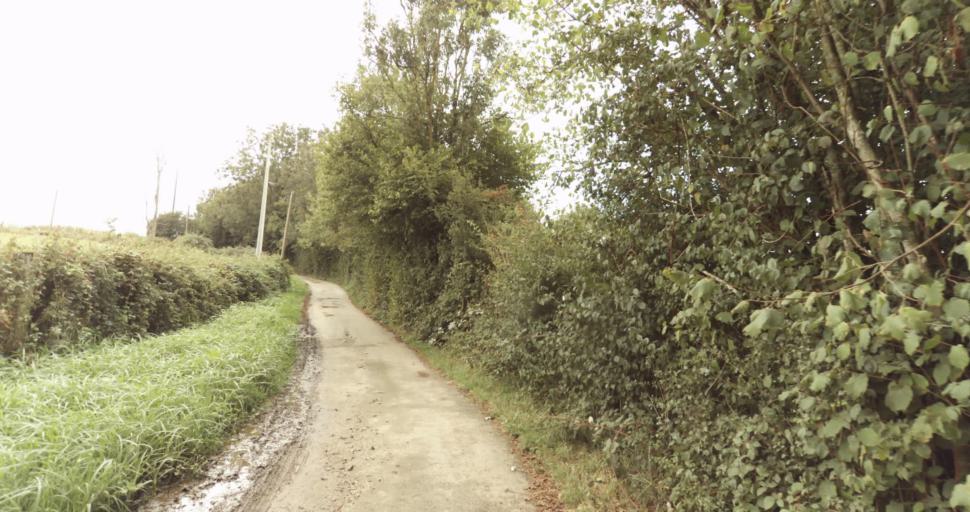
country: FR
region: Lower Normandy
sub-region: Departement de l'Orne
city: Sainte-Gauburge-Sainte-Colombe
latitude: 48.7053
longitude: 0.3421
